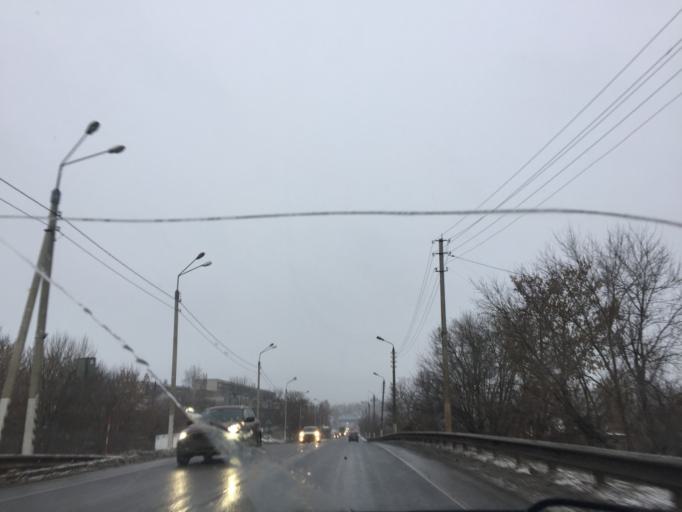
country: RU
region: Tula
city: Plavsk
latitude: 53.7166
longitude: 37.2973
